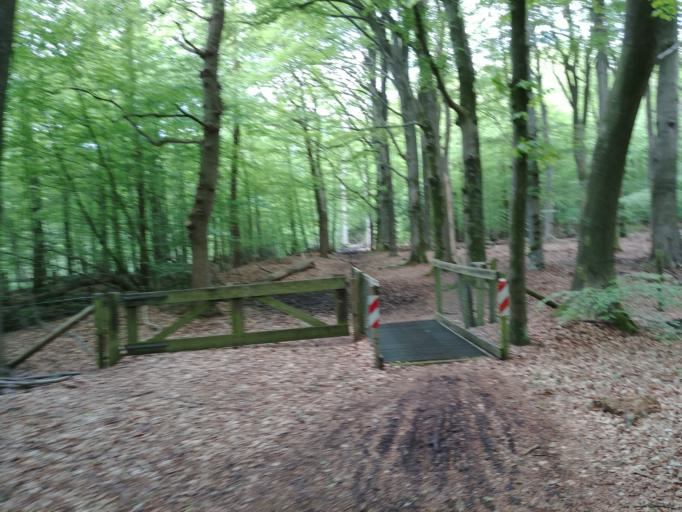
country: NL
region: Gelderland
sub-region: Gemeente Apeldoorn
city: Uddel
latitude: 52.3042
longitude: 5.7228
